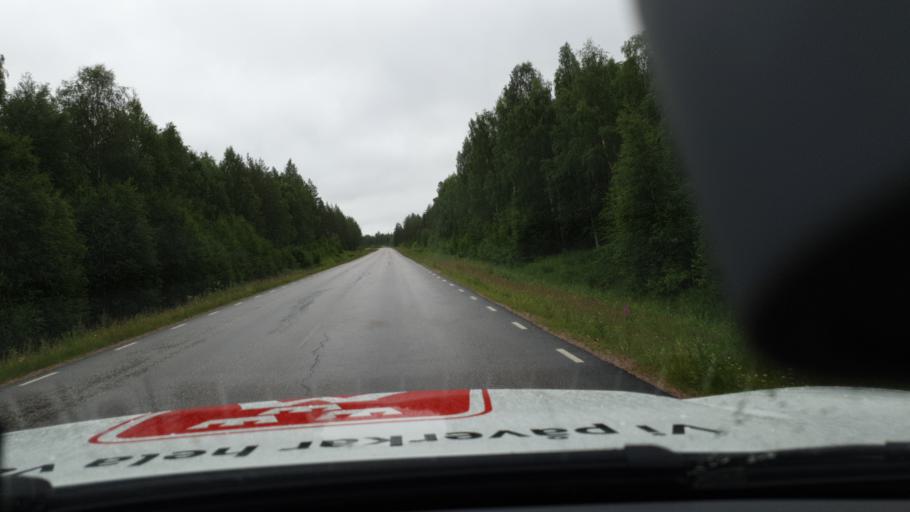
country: SE
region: Norrbotten
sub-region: Overtornea Kommun
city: OEvertornea
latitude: 66.4773
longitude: 23.6876
